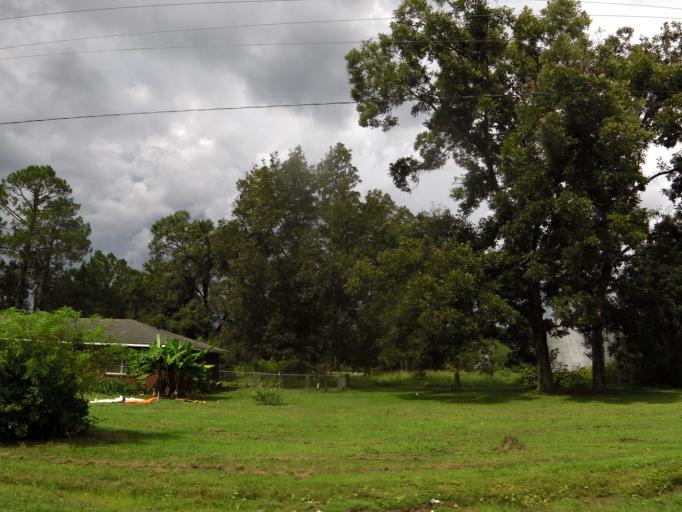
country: US
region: Georgia
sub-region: Brantley County
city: Nahunta
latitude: 31.2031
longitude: -81.9836
